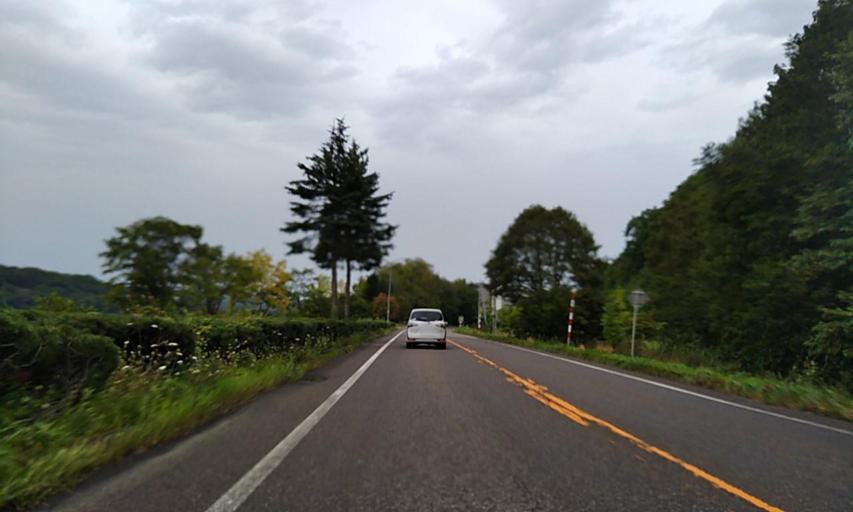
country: JP
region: Hokkaido
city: Abashiri
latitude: 43.9788
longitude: 144.2164
